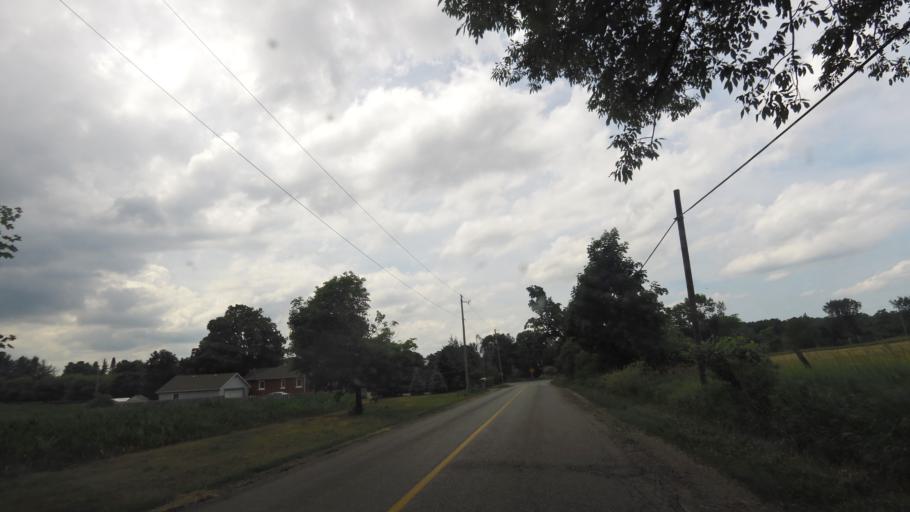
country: CA
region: Ontario
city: Brampton
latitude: 43.8384
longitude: -79.8715
